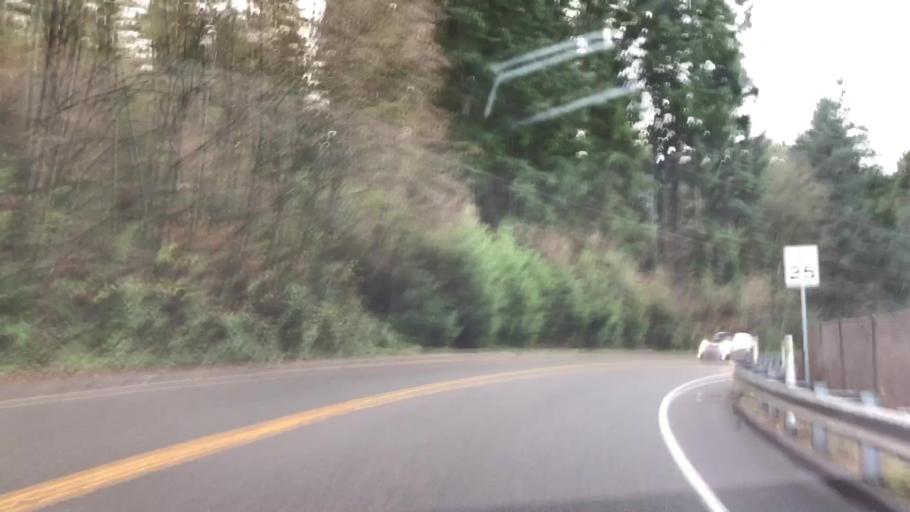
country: US
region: Washington
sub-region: King County
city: Issaquah
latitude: 47.5302
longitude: -122.0238
